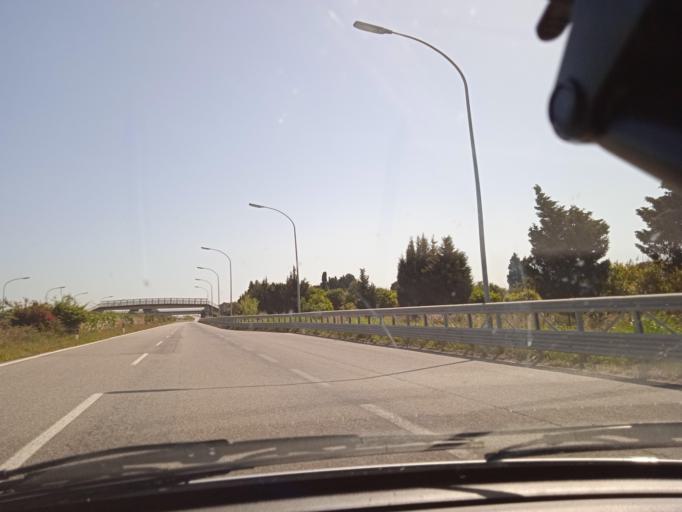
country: IT
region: Sicily
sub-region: Messina
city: Barcellona Pozzo di Gotto
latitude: 38.1572
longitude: 15.1902
